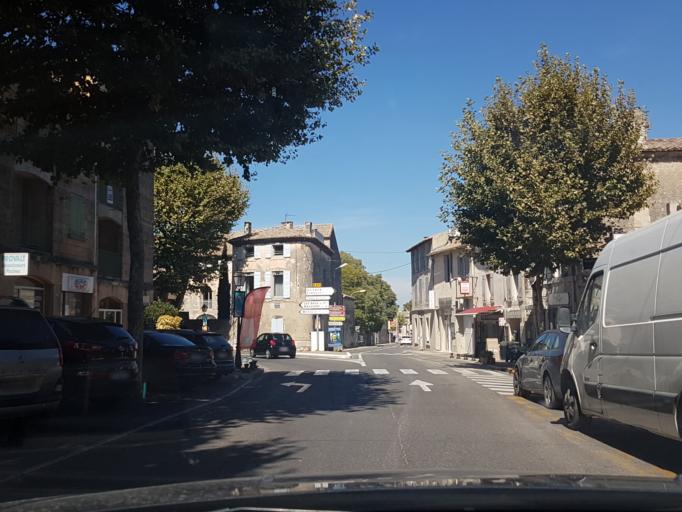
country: FR
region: Provence-Alpes-Cote d'Azur
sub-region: Departement des Bouches-du-Rhone
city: Saint-Remy-de-Provence
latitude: 43.7898
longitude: 4.8334
